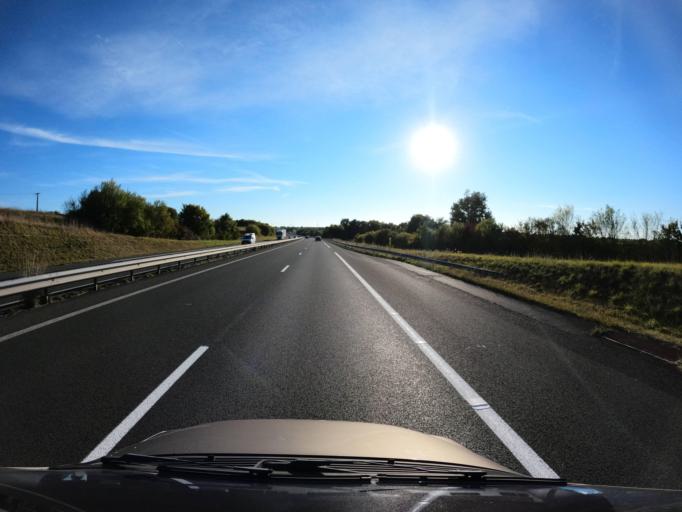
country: FR
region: Pays de la Loire
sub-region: Departement de Maine-et-Loire
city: Chemille-Melay
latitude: 47.2300
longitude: -0.7527
